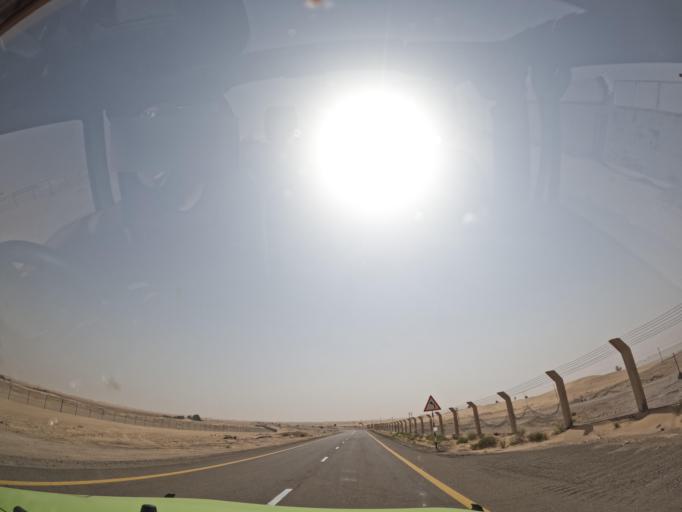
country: OM
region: Al Buraimi
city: Al Buraymi
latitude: 24.6375
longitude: 55.4861
